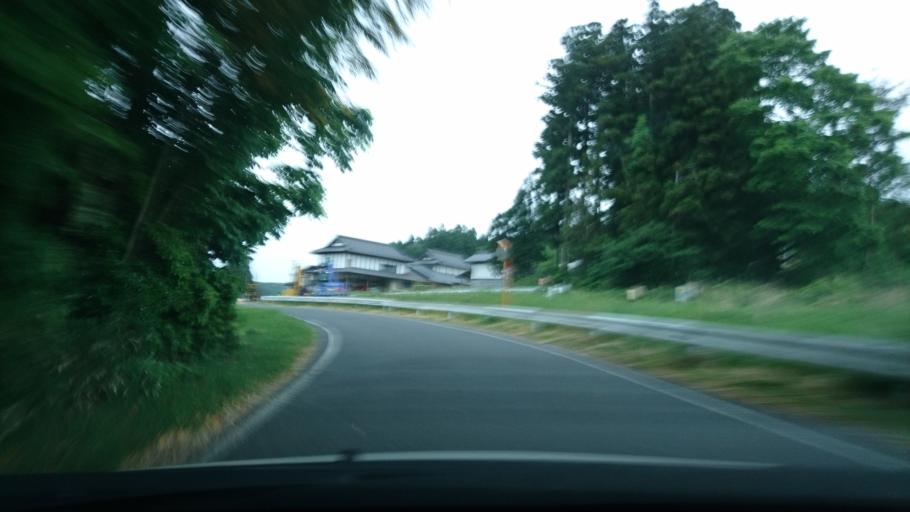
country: JP
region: Iwate
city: Ichinoseki
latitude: 38.9160
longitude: 141.1747
